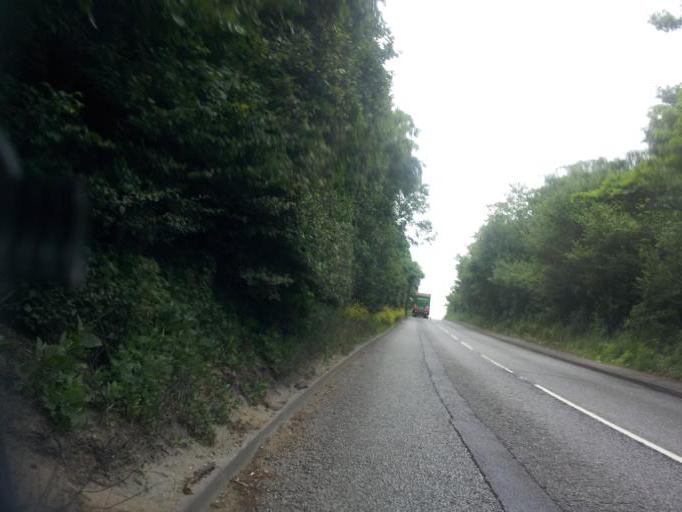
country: GB
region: England
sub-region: Kent
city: Aylesford
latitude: 51.3001
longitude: 0.5029
